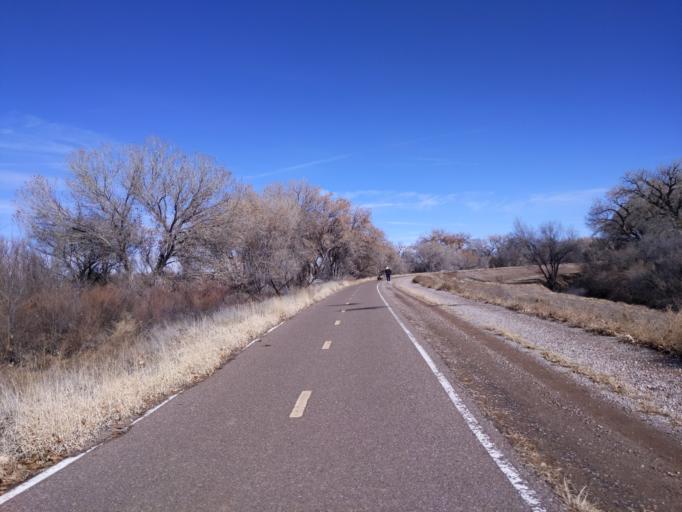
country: US
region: New Mexico
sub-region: Bernalillo County
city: Lee Acres
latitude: 35.1596
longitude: -106.6666
